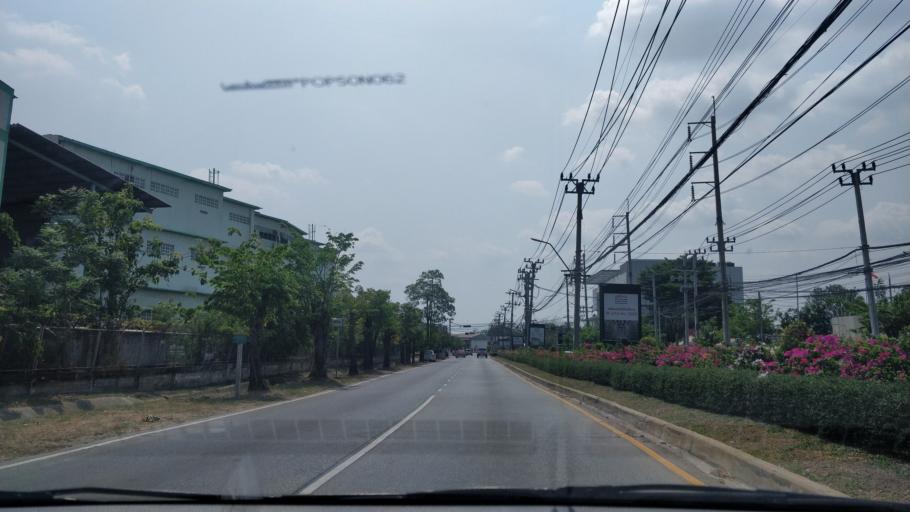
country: TH
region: Bangkok
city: Lat Krabang
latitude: 13.7578
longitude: 100.7914
